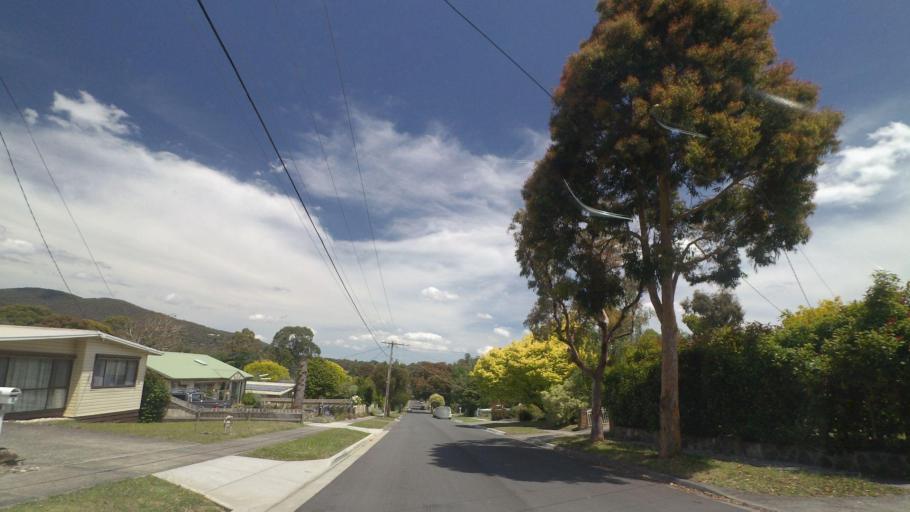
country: AU
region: Victoria
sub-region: Knox
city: Boronia
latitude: -37.8479
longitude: 145.2933
